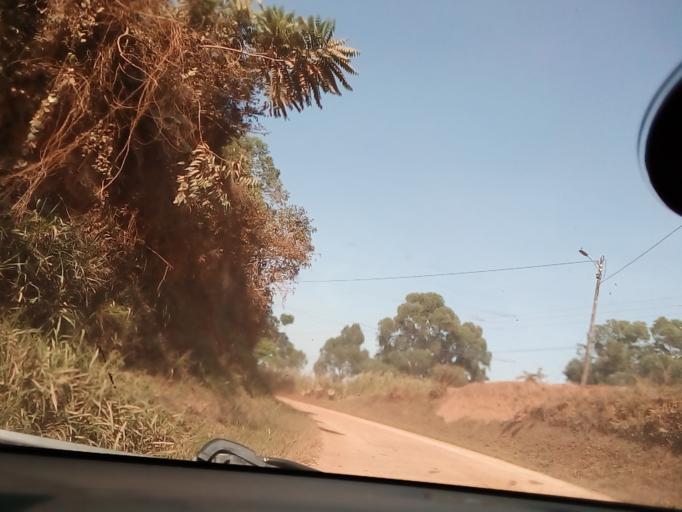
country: UG
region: Central Region
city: Masaka
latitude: -0.3302
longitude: 31.7359
